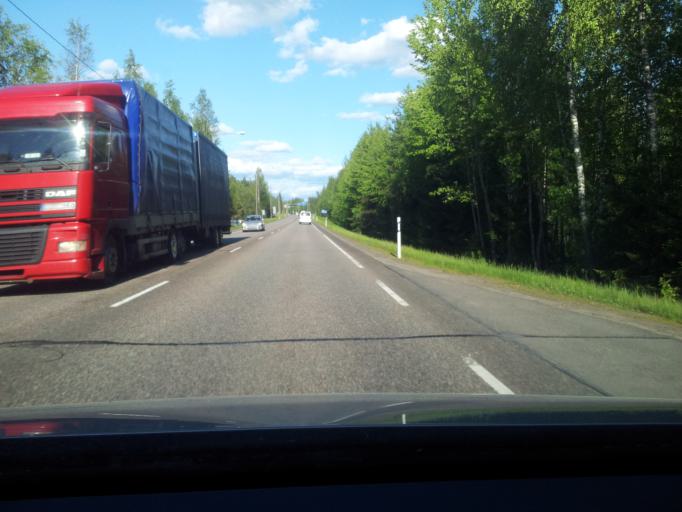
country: FI
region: Kymenlaakso
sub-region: Kouvola
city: Kouvola
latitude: 60.8861
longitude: 26.8249
